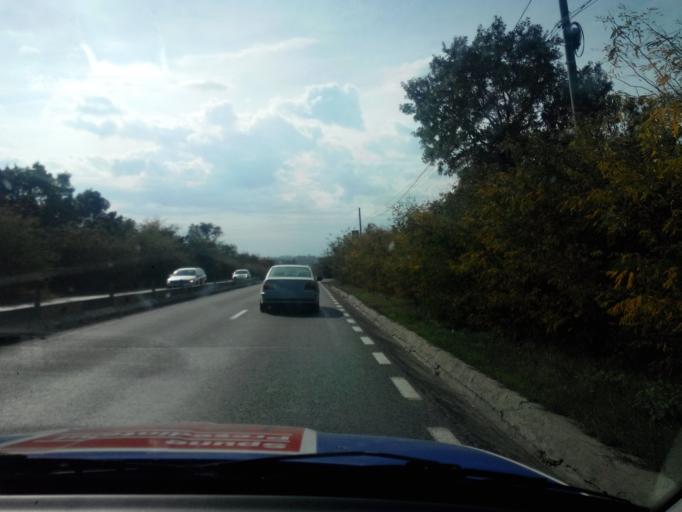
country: RO
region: Constanta
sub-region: Comuna Agigea
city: Agigea
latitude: 44.1242
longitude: 28.6138
